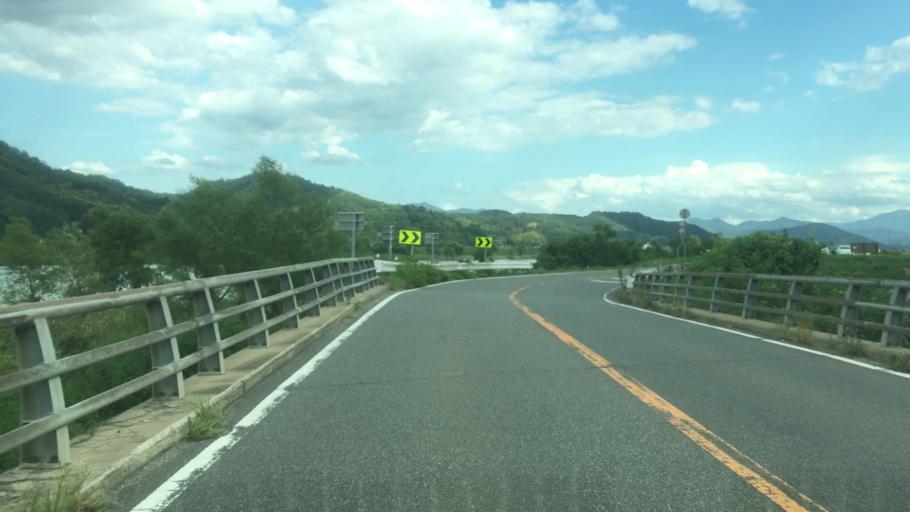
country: JP
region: Hyogo
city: Toyooka
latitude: 35.5743
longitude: 134.8059
